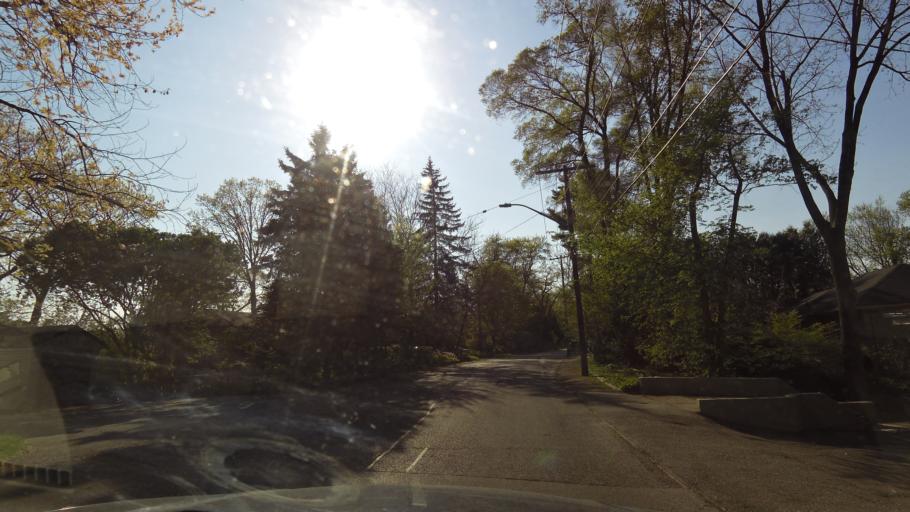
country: CA
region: Ontario
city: Mississauga
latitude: 43.5538
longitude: -79.5954
